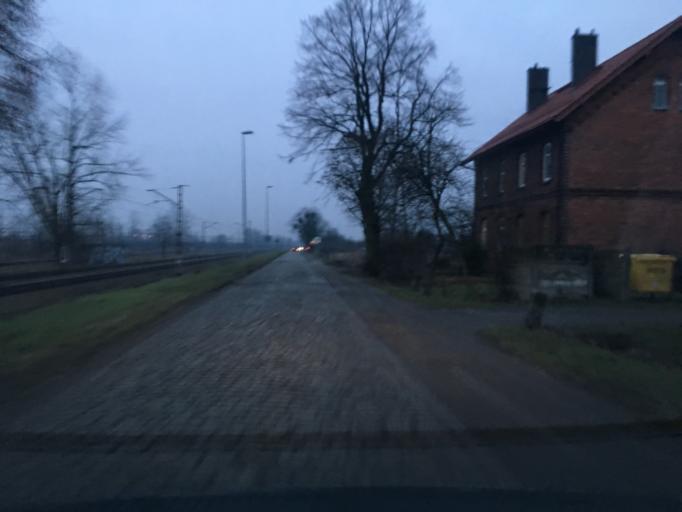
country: PL
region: Lower Silesian Voivodeship
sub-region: Powiat wroclawski
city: Radwanice
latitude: 51.0514
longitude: 17.0956
